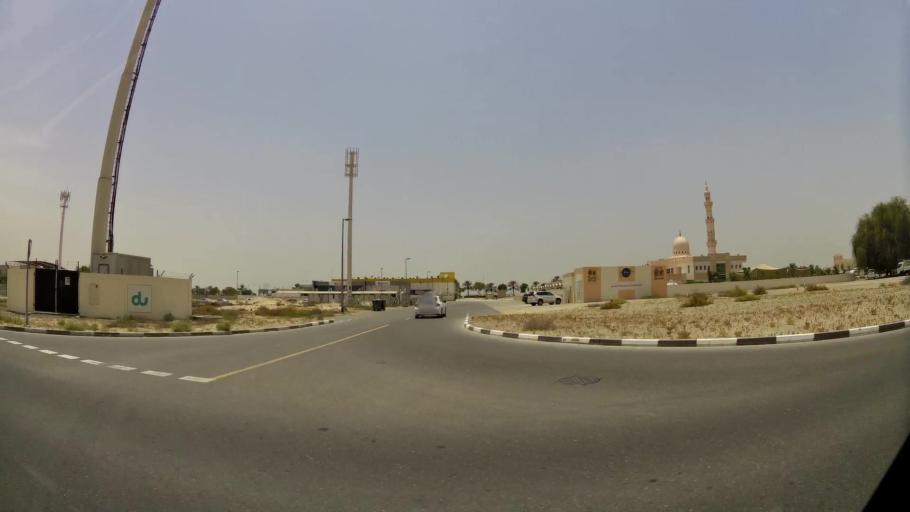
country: AE
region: Ash Shariqah
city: Sharjah
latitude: 25.2015
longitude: 55.3792
